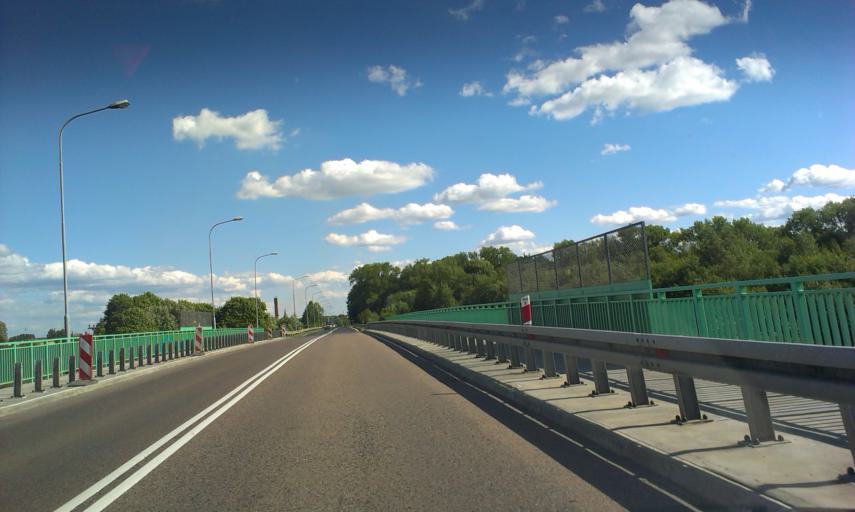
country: PL
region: West Pomeranian Voivodeship
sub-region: Powiat szczecinecki
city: Szczecinek
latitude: 53.7274
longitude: 16.6746
